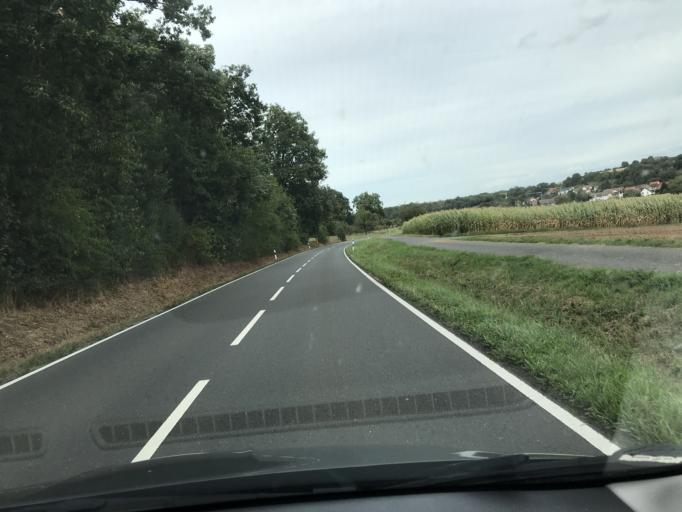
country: DE
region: Hesse
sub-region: Regierungsbezirk Darmstadt
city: Schaafheim
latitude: 49.9097
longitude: 8.9633
